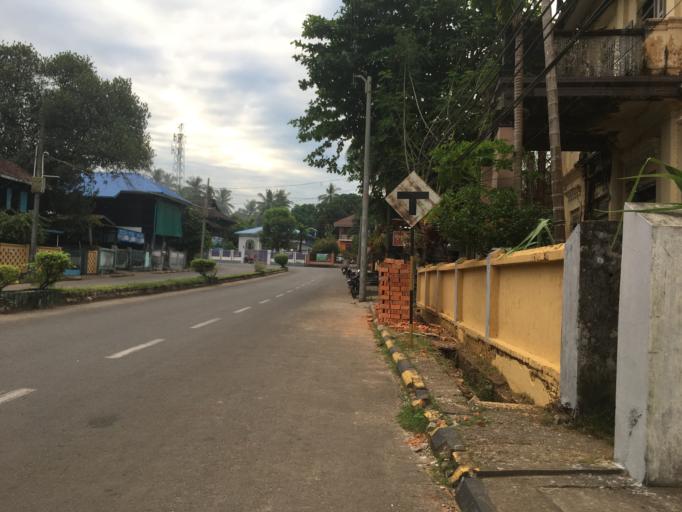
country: MM
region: Mon
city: Mawlamyine
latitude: 16.4713
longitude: 97.6232
